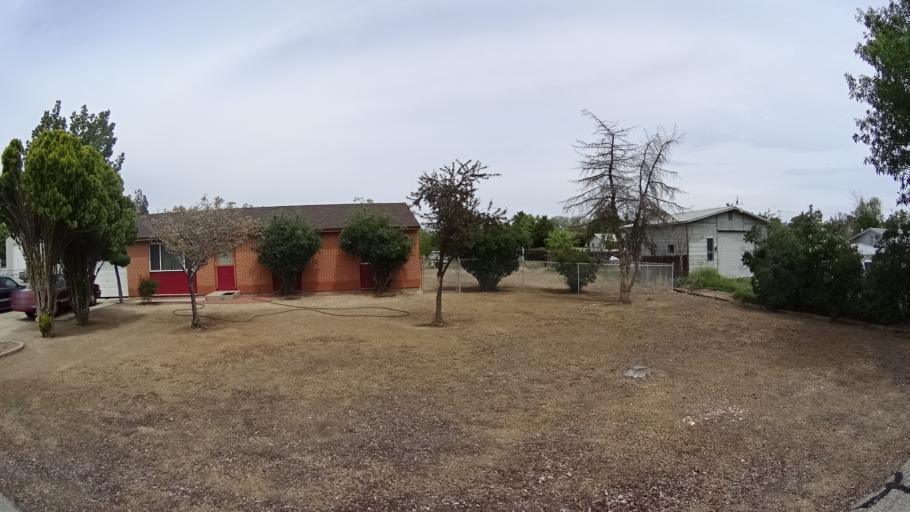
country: US
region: Idaho
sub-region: Ada County
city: Meridian
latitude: 43.5329
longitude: -116.3167
